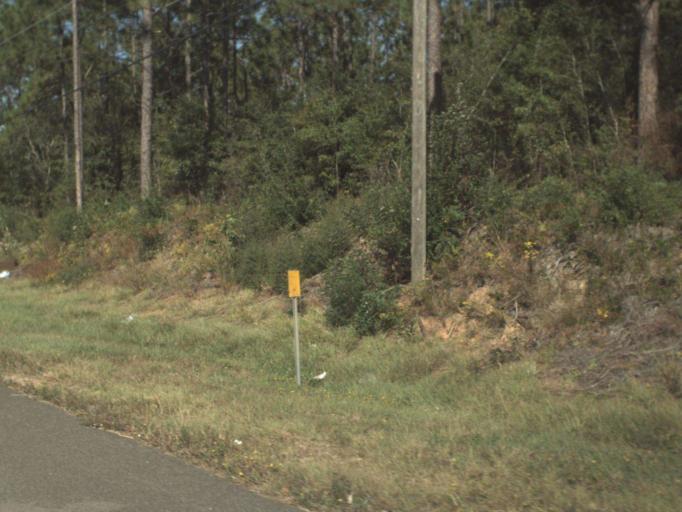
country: US
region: Florida
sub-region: Okaloosa County
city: Crestview
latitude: 30.7564
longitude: -86.5311
